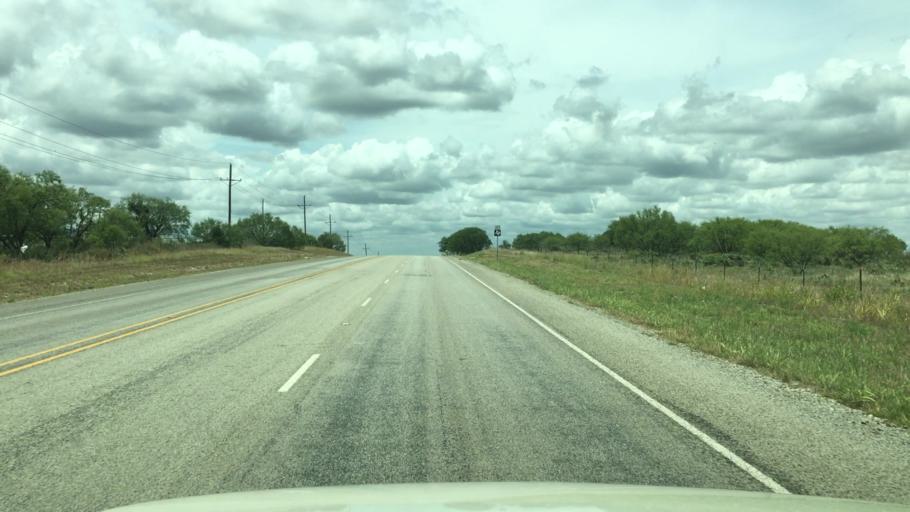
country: US
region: Texas
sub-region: McCulloch County
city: Brady
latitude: 31.0025
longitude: -99.1800
